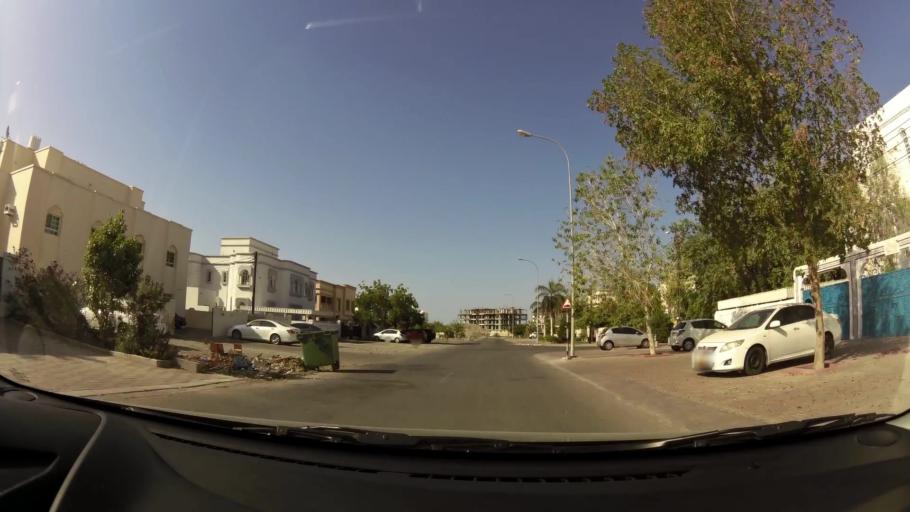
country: OM
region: Muhafazat Masqat
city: As Sib al Jadidah
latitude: 23.6186
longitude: 58.2092
